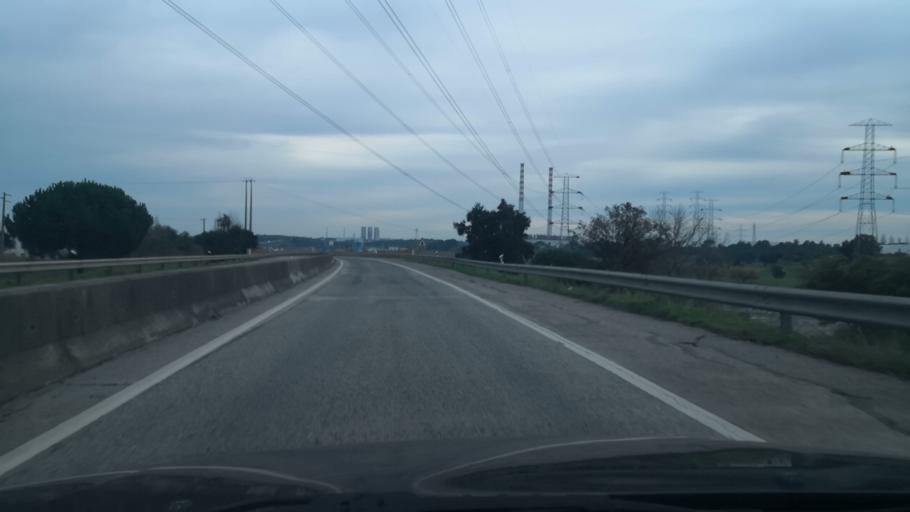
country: PT
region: Setubal
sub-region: Setubal
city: Setubal
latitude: 38.5250
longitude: -8.8437
